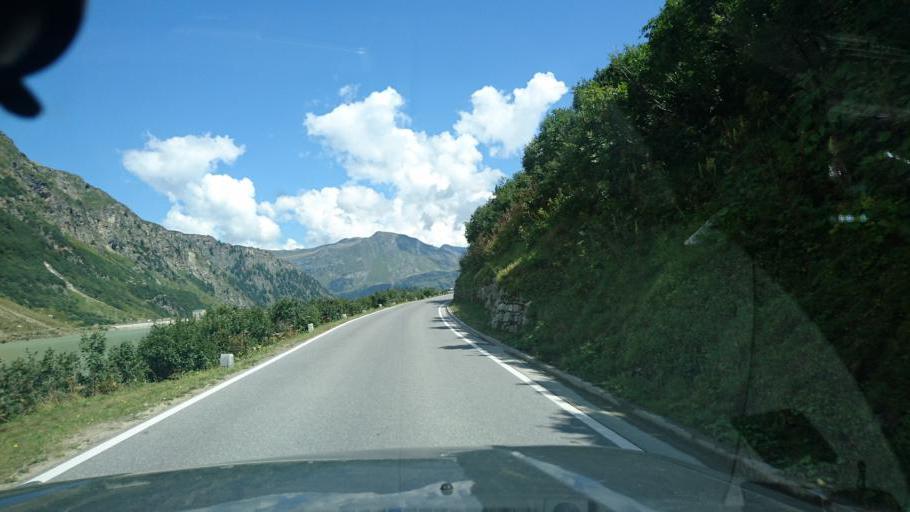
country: AT
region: Vorarlberg
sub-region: Politischer Bezirk Bludenz
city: Gaschurn
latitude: 46.9299
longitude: 10.0556
